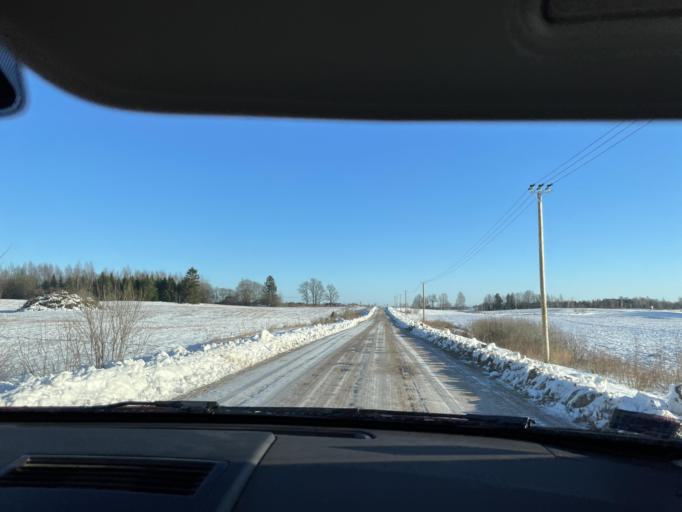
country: LV
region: Ludzas Rajons
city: Ludza
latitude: 56.4611
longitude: 27.6257
